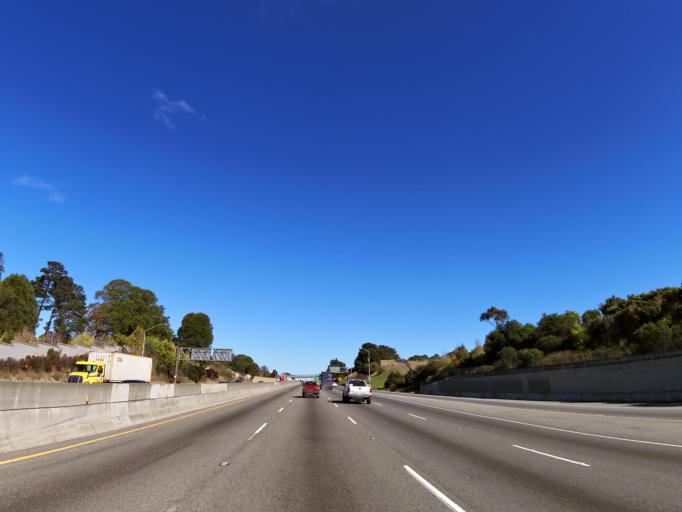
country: US
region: California
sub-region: Contra Costa County
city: Rollingwood
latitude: 37.9685
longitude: -122.3210
